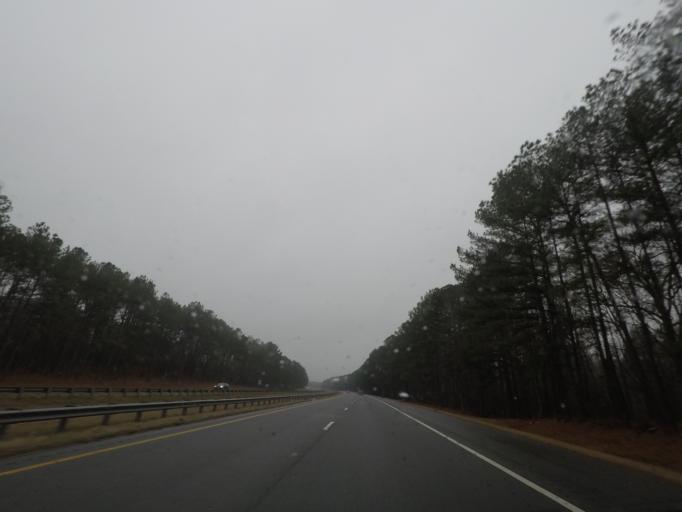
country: US
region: North Carolina
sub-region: Chatham County
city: Farmville
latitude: 35.5706
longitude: -79.1446
